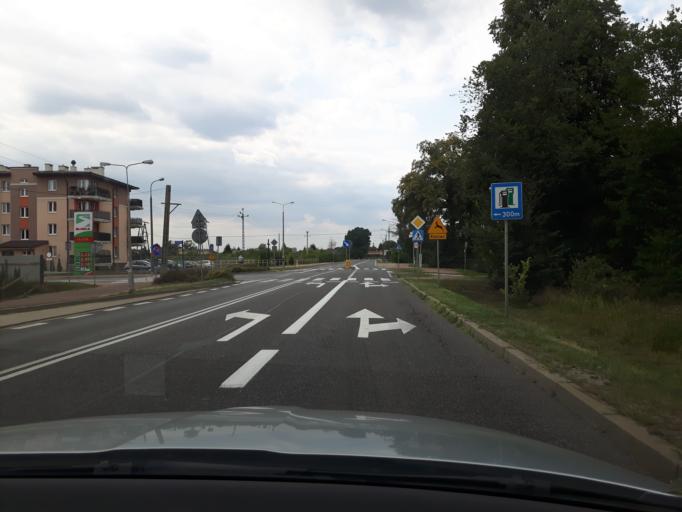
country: PL
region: Masovian Voivodeship
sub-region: Powiat legionowski
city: Wieliszew
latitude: 52.4480
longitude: 20.9782
